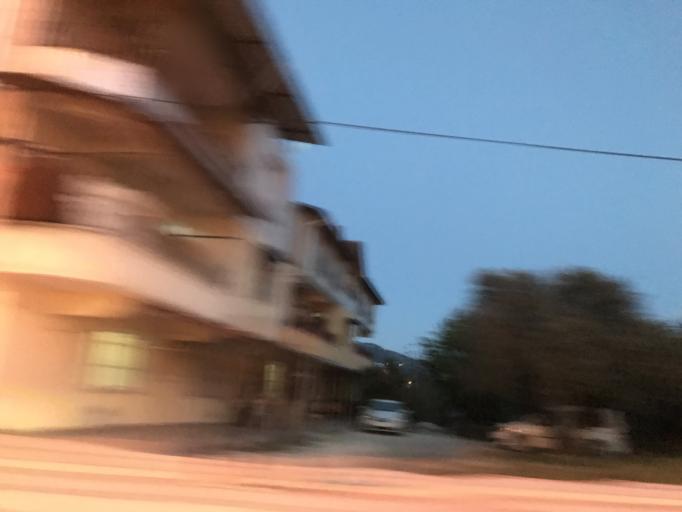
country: TR
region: Hatay
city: Asagiokcular
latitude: 36.1868
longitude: 36.1229
